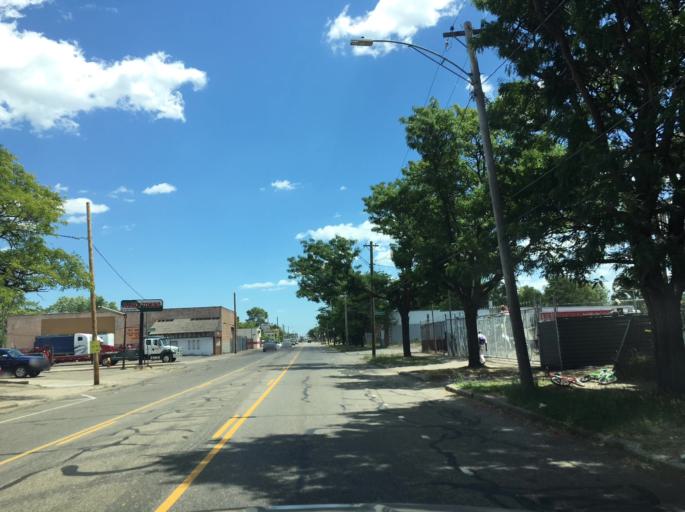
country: US
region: Michigan
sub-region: Wayne County
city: Hamtramck
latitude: 42.4189
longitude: -83.0504
